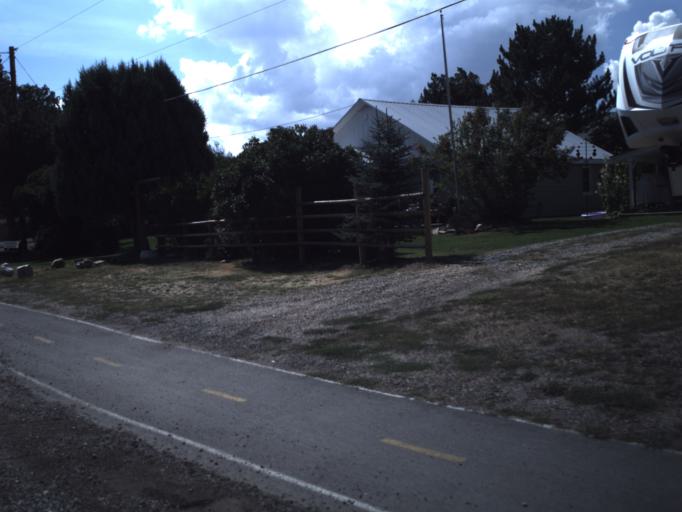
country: US
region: Idaho
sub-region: Bear Lake County
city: Paris
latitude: 41.9190
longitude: -111.3932
